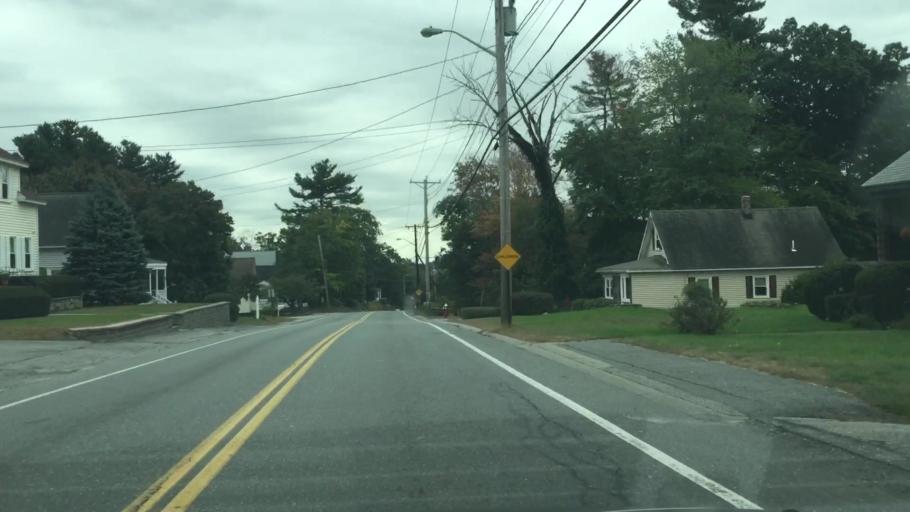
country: US
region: Massachusetts
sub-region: Middlesex County
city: Lowell
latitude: 42.6630
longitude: -71.3460
